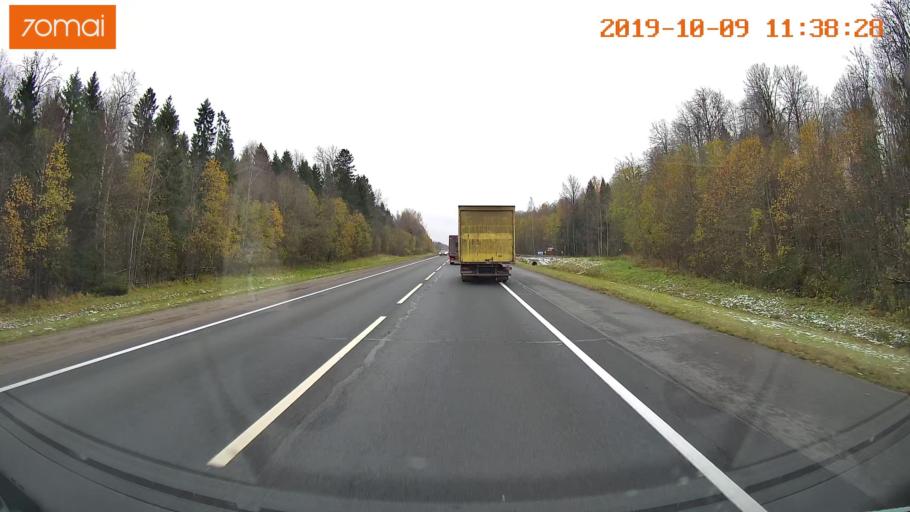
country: RU
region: Vologda
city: Gryazovets
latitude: 58.9679
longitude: 40.1560
